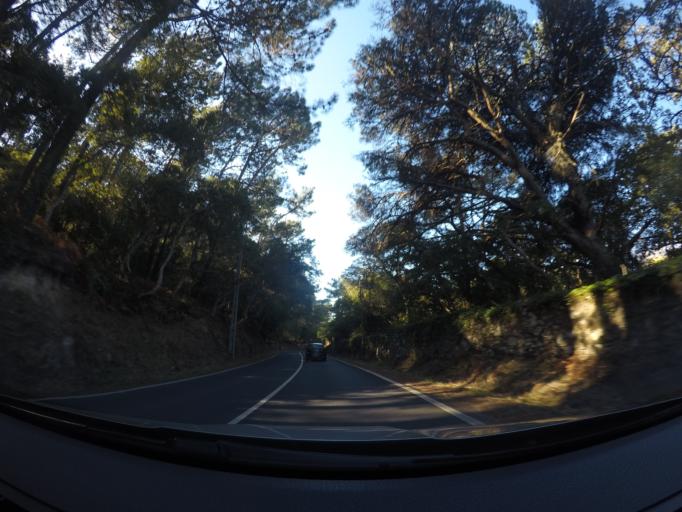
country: PT
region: Lisbon
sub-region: Sintra
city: Colares
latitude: 38.7846
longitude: -9.4681
